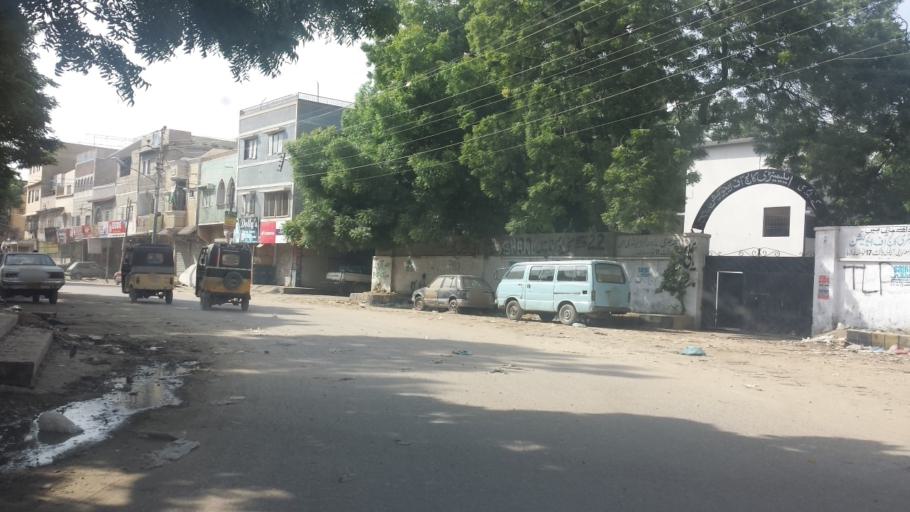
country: PK
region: Sindh
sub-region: Karachi District
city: Karachi
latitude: 24.9445
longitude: 67.0771
